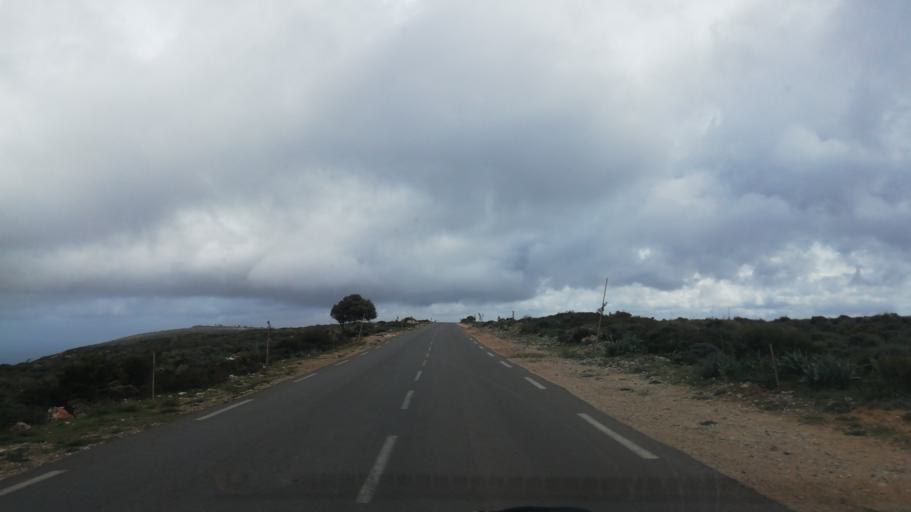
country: DZ
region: Oran
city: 'Ain el Turk
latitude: 35.6994
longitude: -0.7570
